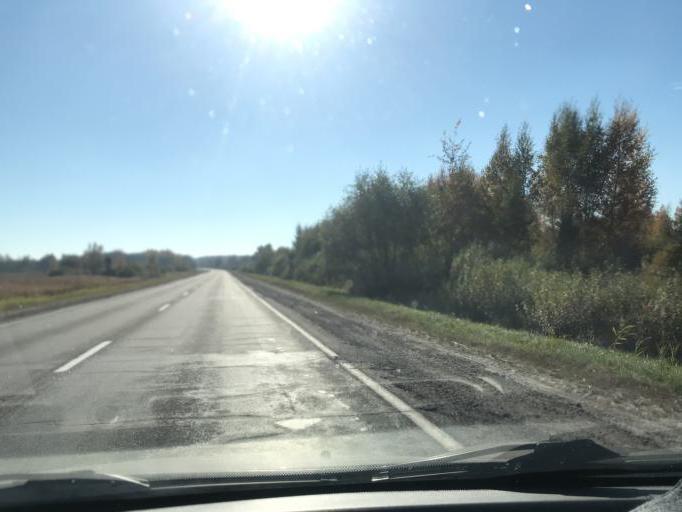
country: BY
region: Gomel
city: Kastsyukowka
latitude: 52.4481
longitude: 30.8250
